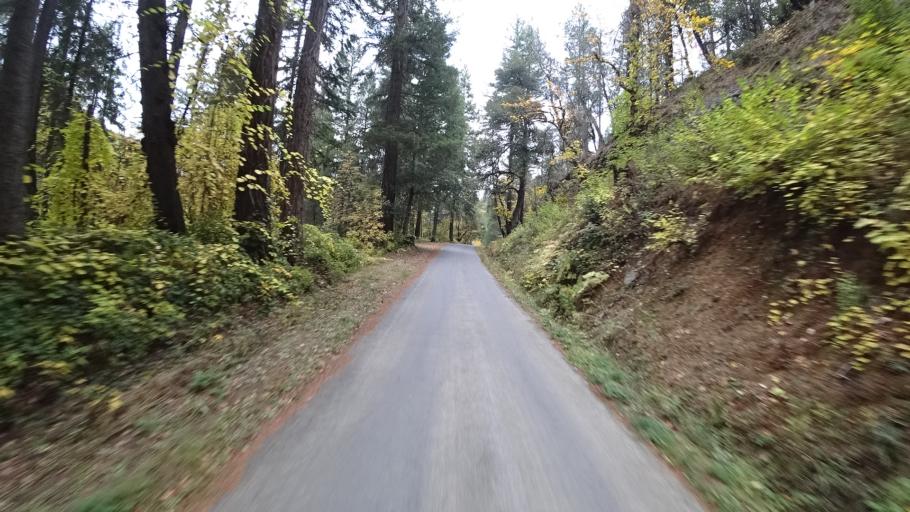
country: US
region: California
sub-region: Siskiyou County
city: Happy Camp
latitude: 41.7700
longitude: -123.3374
